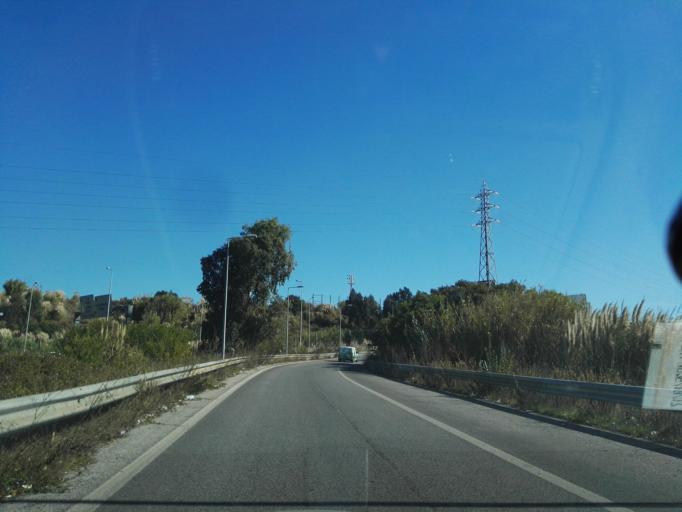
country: PT
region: Lisbon
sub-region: Sintra
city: Rio de Mouro
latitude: 38.7758
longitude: -9.3228
